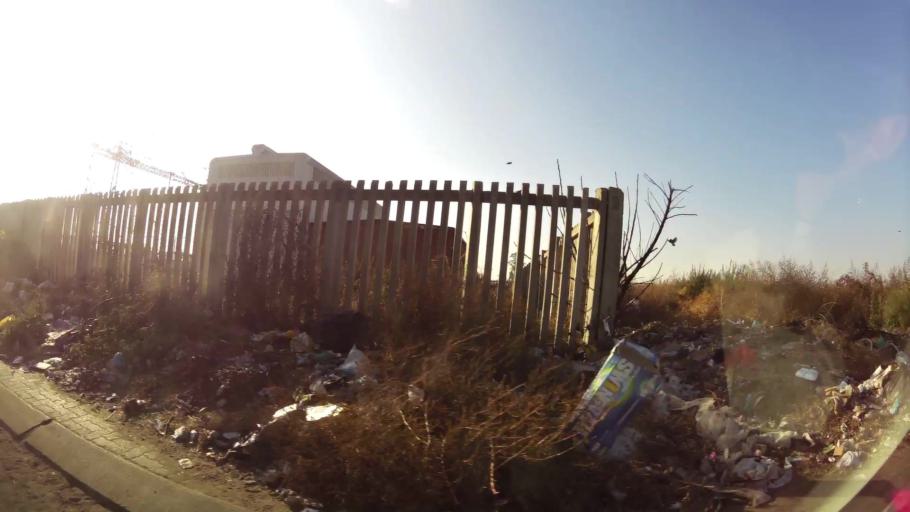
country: ZA
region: Orange Free State
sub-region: Mangaung Metropolitan Municipality
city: Bloemfontein
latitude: -29.1346
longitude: 26.2527
